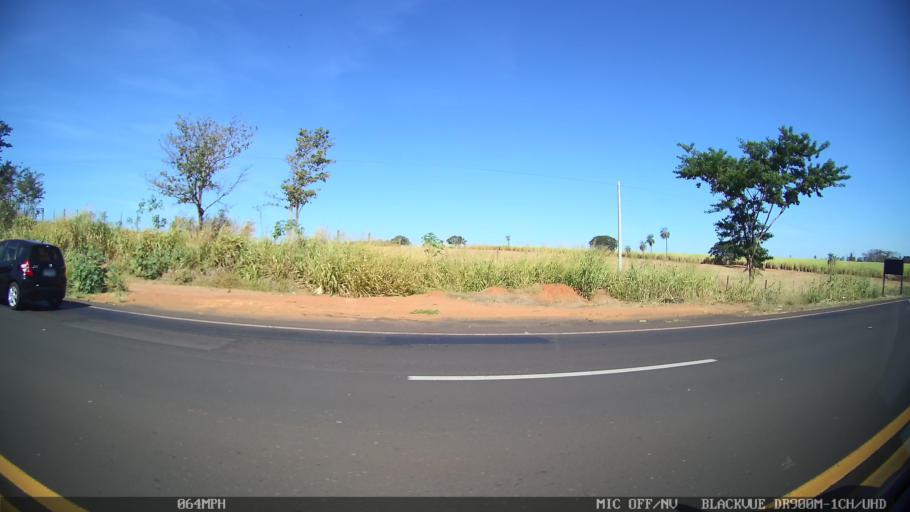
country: BR
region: Sao Paulo
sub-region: Barretos
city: Barretos
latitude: -20.6056
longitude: -48.7389
